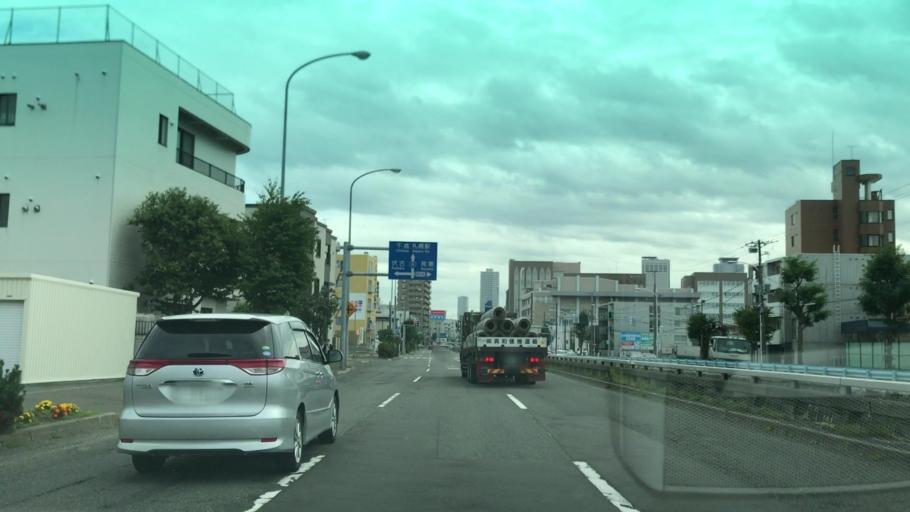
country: JP
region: Hokkaido
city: Sapporo
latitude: 43.0833
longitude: 141.3499
